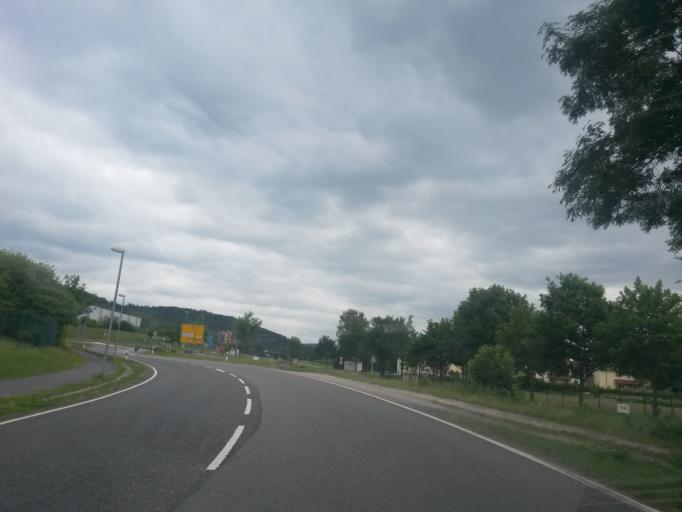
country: DE
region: Hesse
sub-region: Regierungsbezirk Kassel
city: Bad Hersfeld
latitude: 50.8443
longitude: 9.6803
